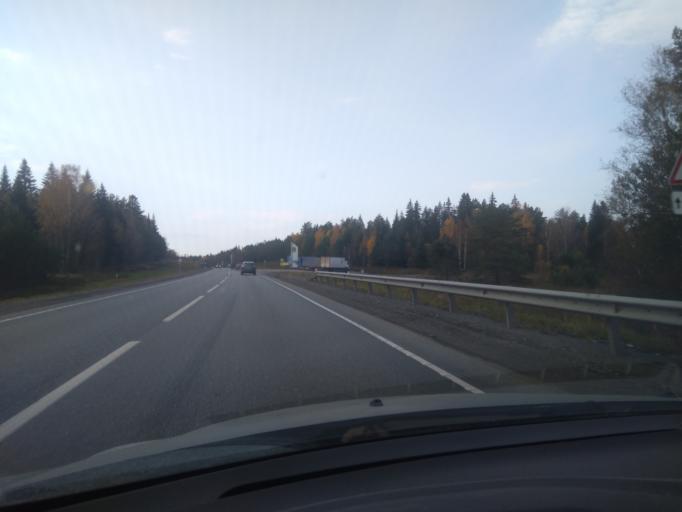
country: RU
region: Sverdlovsk
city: Druzhinino
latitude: 56.8216
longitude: 59.5713
